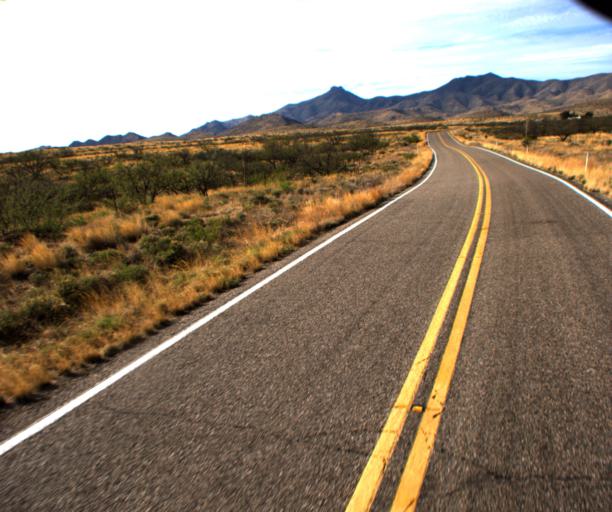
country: US
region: Arizona
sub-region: Cochise County
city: Willcox
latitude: 32.1250
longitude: -109.5561
